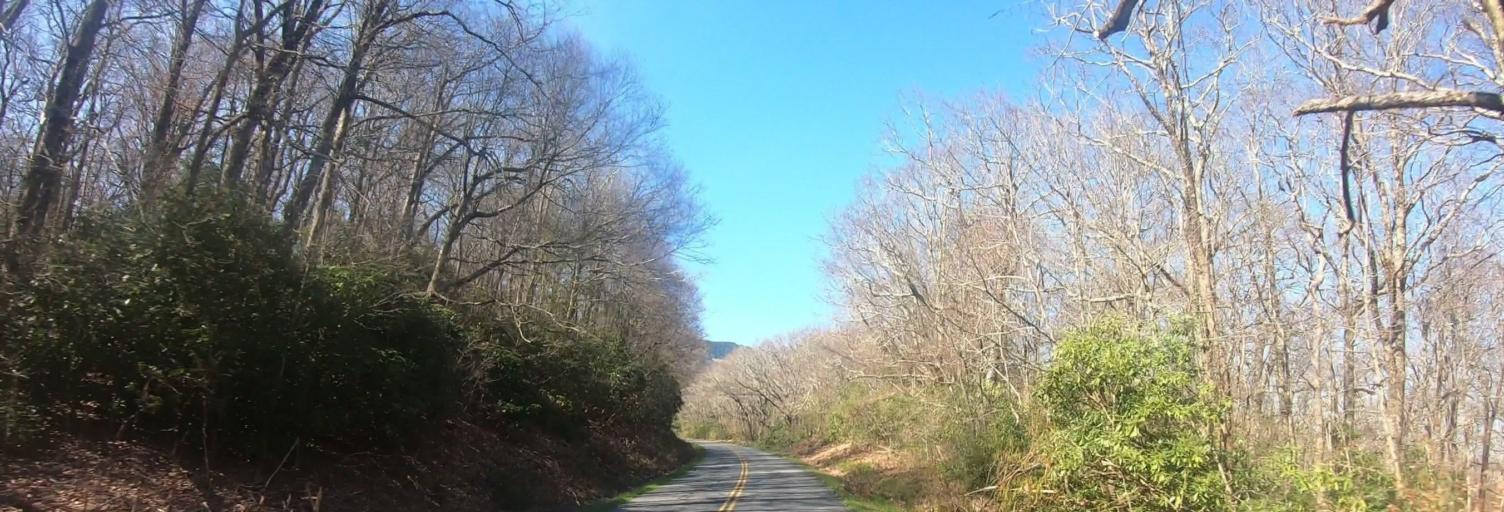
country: US
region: North Carolina
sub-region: Avery County
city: Banner Elk
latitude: 36.0776
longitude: -81.8340
